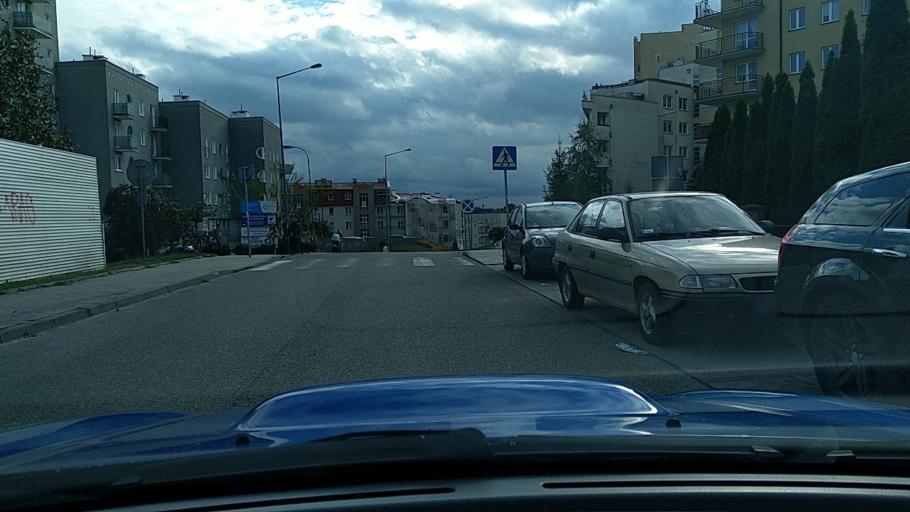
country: PL
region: Warmian-Masurian Voivodeship
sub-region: Powiat olsztynski
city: Olsztyn
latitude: 53.7637
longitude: 20.4894
